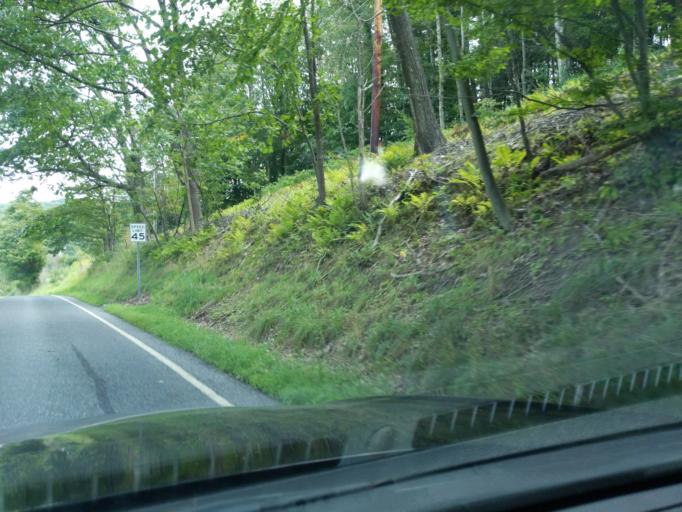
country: US
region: Pennsylvania
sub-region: Blair County
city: Duncansville
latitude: 40.3695
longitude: -78.5016
